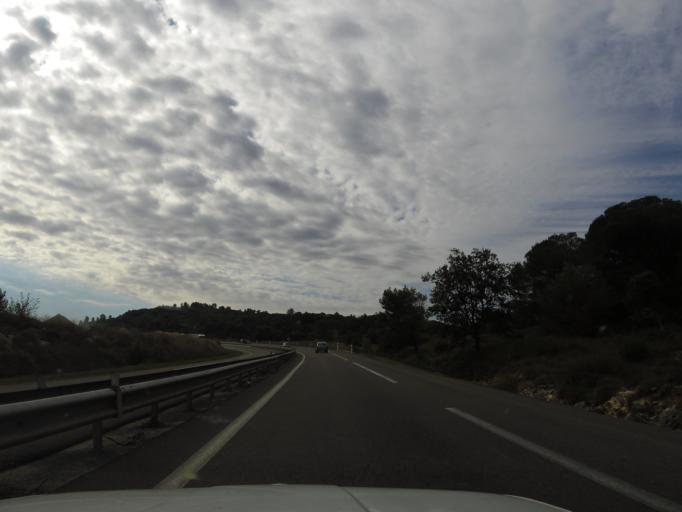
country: FR
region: Languedoc-Roussillon
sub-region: Departement du Gard
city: La Calmette
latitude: 43.9099
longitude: 4.2698
